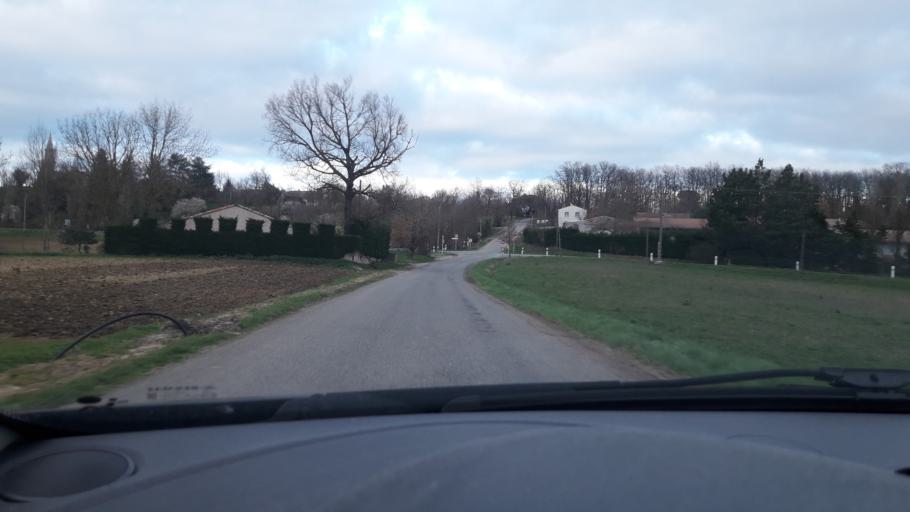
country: FR
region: Midi-Pyrenees
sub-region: Departement de la Haute-Garonne
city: Launac
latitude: 43.7201
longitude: 1.0974
